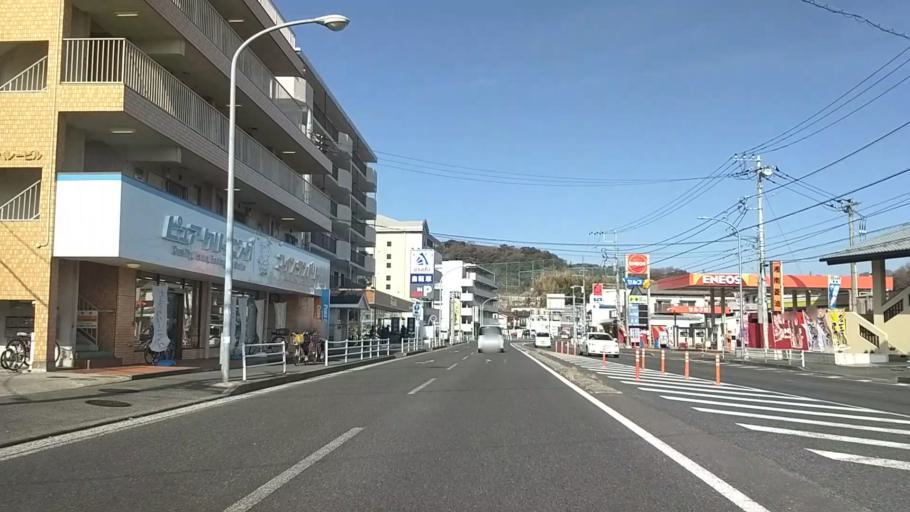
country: JP
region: Kanagawa
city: Zushi
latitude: 35.3456
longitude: 139.6099
